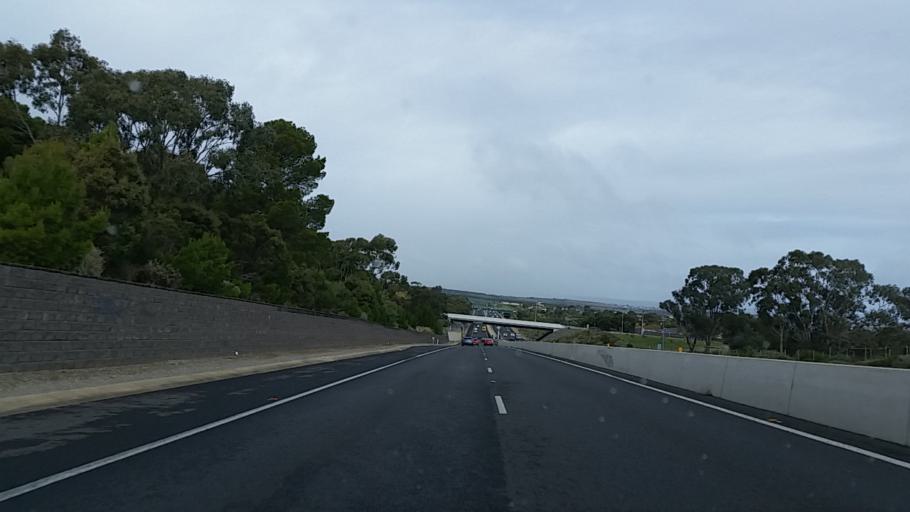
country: AU
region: South Australia
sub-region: Onkaparinga
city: Noarlunga Downs
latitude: -35.1454
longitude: 138.5056
